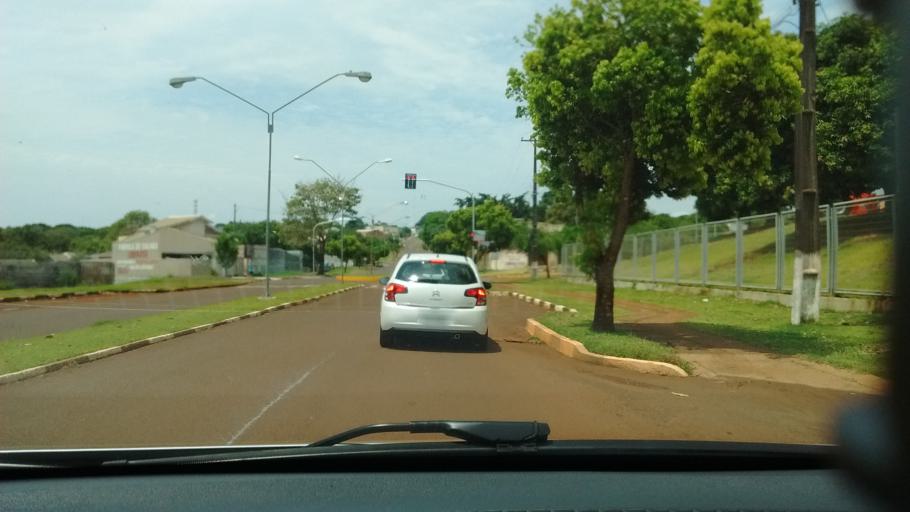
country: BR
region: Parana
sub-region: Corbelia
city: Corbelia
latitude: -24.5510
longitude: -52.9931
